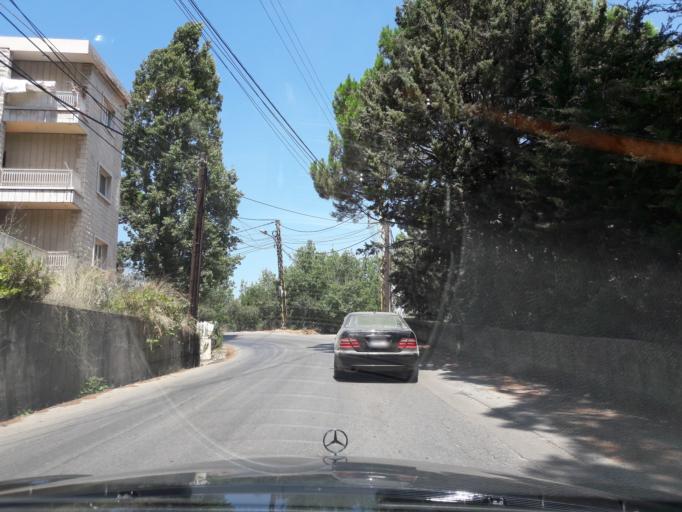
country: LB
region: Mont-Liban
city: Djounie
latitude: 33.9254
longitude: 35.6594
